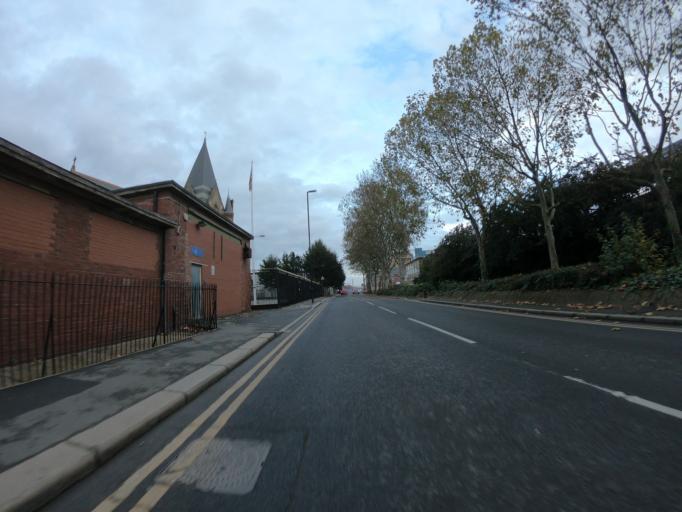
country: GB
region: England
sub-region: Greater London
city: Woolwich
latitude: 51.5025
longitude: 0.0423
